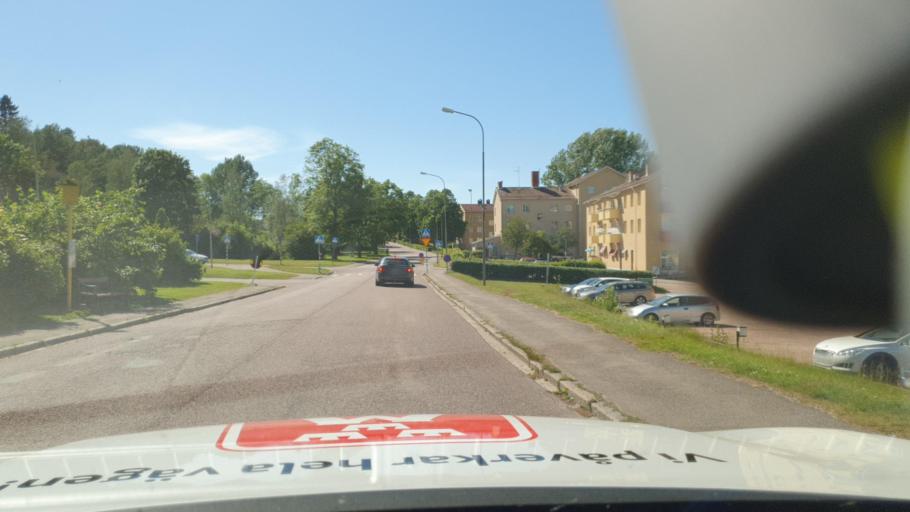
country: SE
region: Vaermland
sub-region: Kristinehamns Kommun
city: Kristinehamn
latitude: 59.3068
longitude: 14.0923
